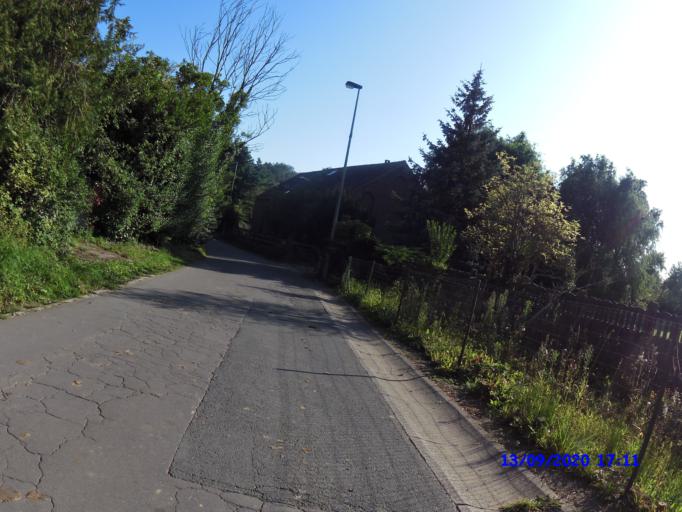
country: BE
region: Flanders
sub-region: Provincie Vlaams-Brabant
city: Dilbeek
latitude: 50.8298
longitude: 4.2617
